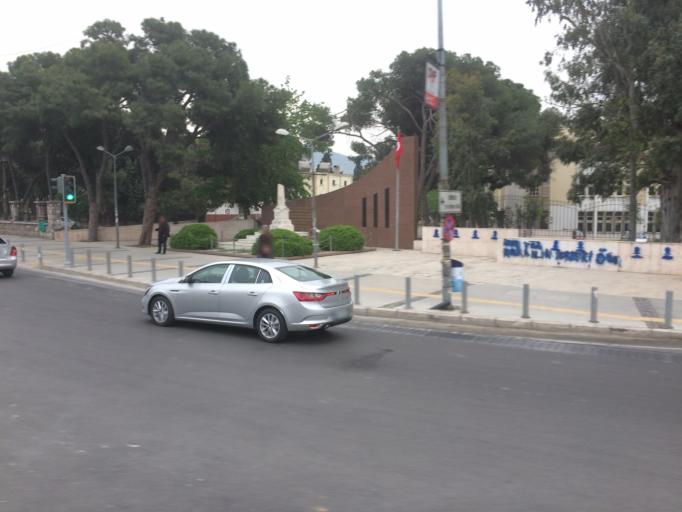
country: TR
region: Izmir
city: Bornova
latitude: 38.4582
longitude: 27.2110
